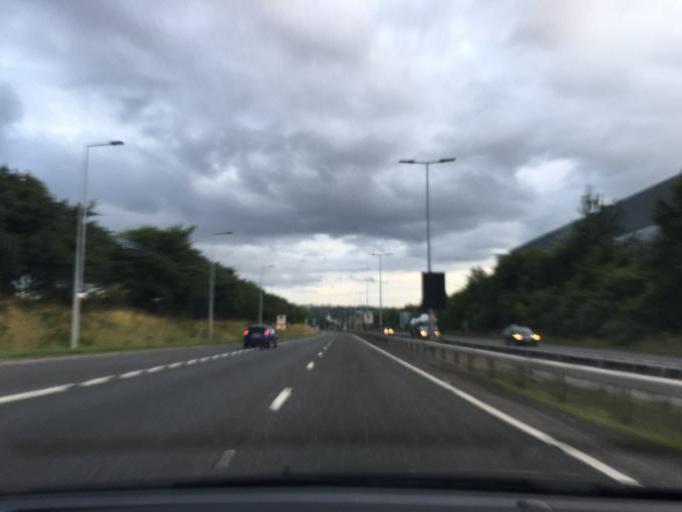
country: GB
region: Scotland
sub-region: Highland
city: Inverness
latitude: 57.4780
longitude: -4.1883
